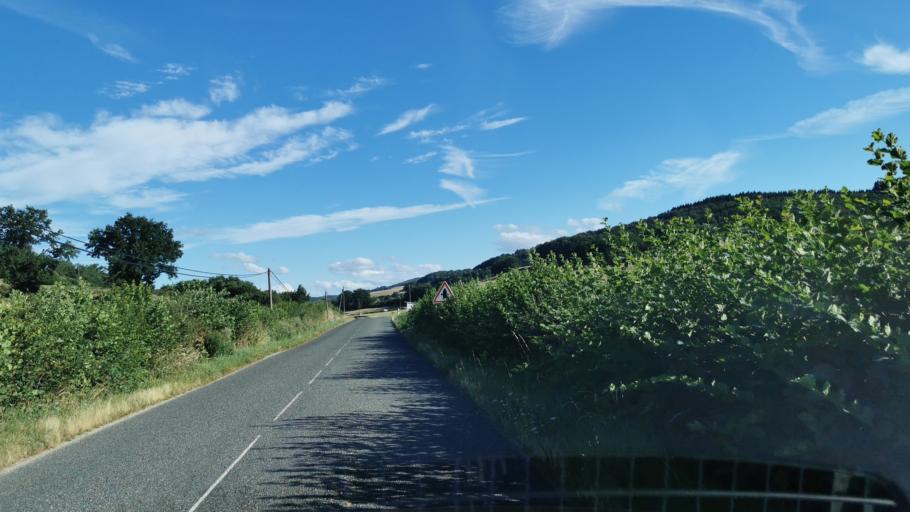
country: FR
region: Bourgogne
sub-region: Departement de Saone-et-Loire
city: Marmagne
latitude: 46.8300
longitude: 4.3178
